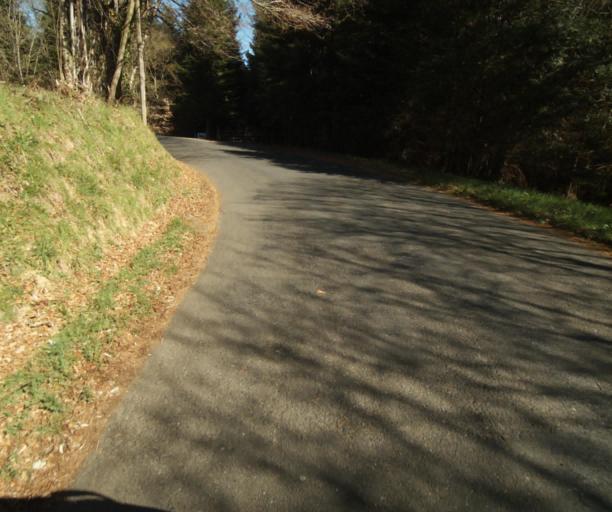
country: FR
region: Limousin
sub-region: Departement de la Correze
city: Uzerche
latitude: 45.4238
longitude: 1.6334
